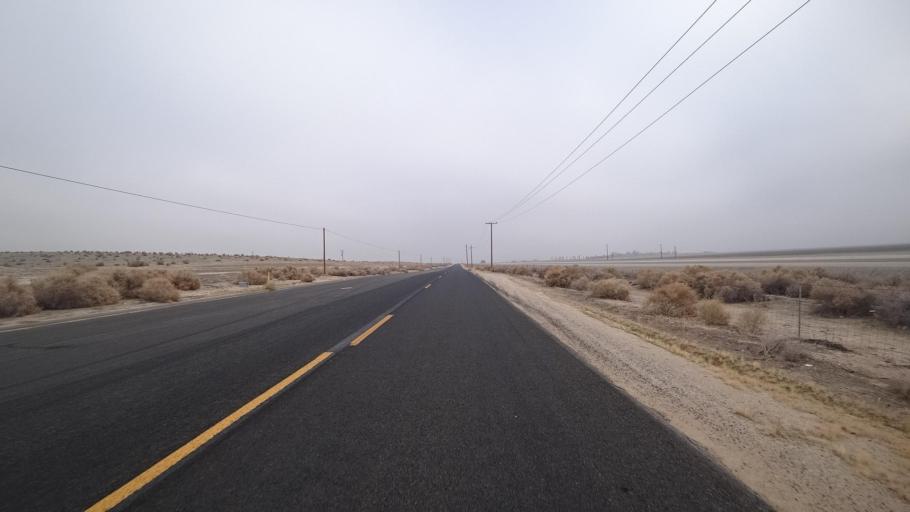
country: US
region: California
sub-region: Kern County
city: Ford City
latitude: 35.2380
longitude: -119.3175
